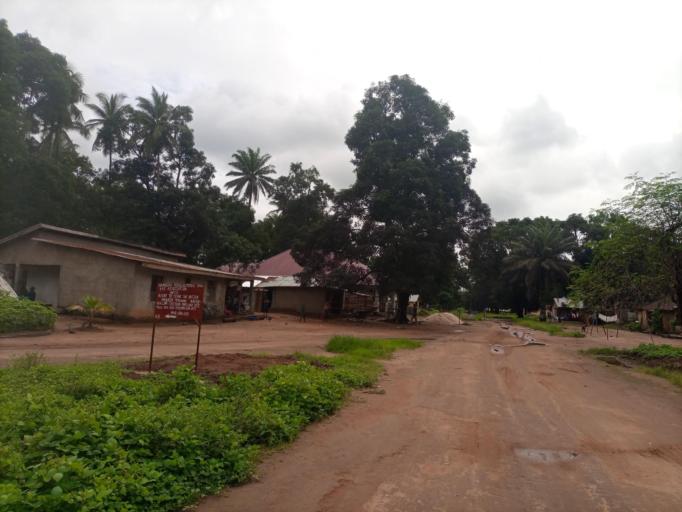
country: SL
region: Northern Province
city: Sawkta
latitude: 8.6372
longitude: -13.1918
